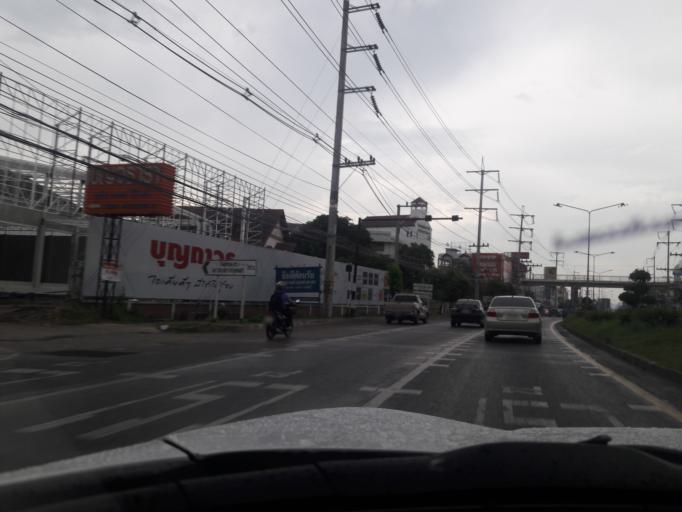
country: TH
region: Lop Buri
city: Lop Buri
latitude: 14.7992
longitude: 100.6611
